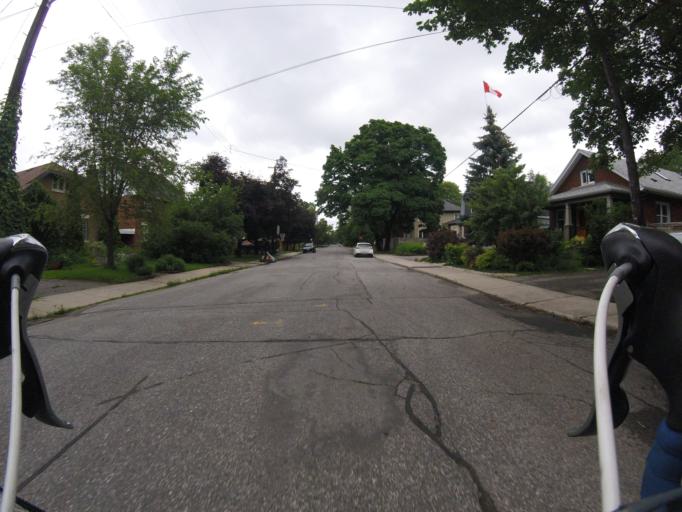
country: CA
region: Ontario
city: Ottawa
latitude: 45.3955
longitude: -75.7364
